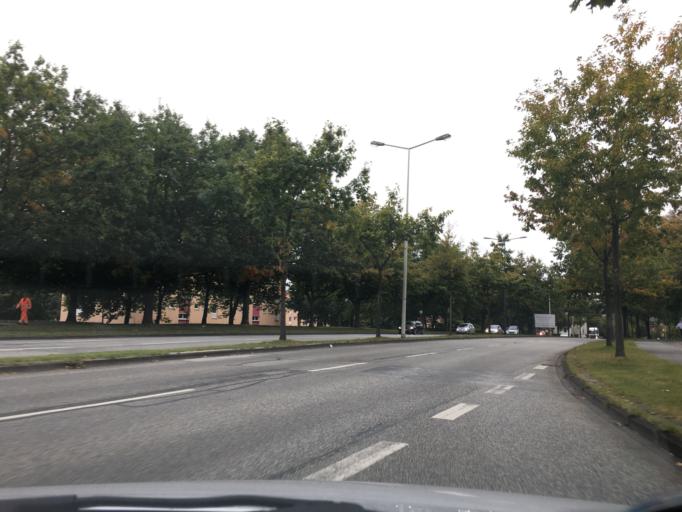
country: DE
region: Schleswig-Holstein
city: Melsdorf
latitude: 54.3176
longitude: 10.0500
